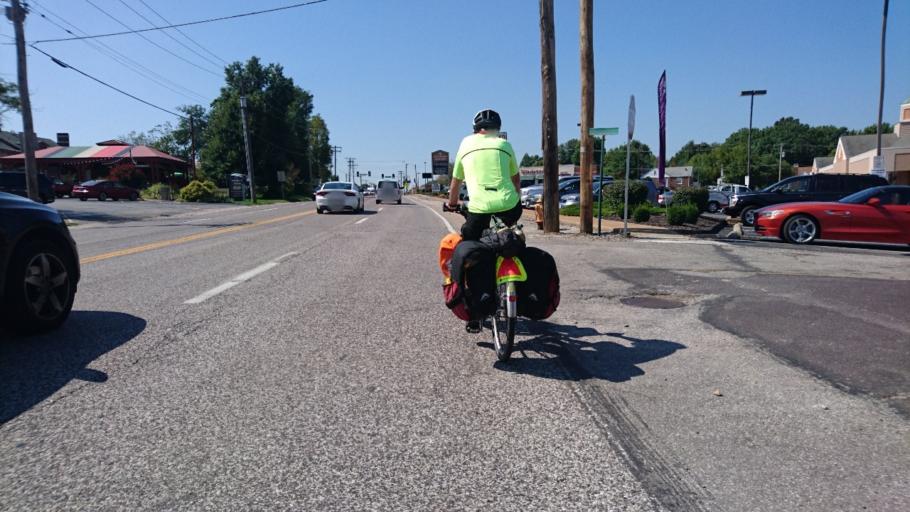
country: US
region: Missouri
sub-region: Saint Louis County
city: Rock Hill
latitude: 38.6078
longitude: -90.3713
